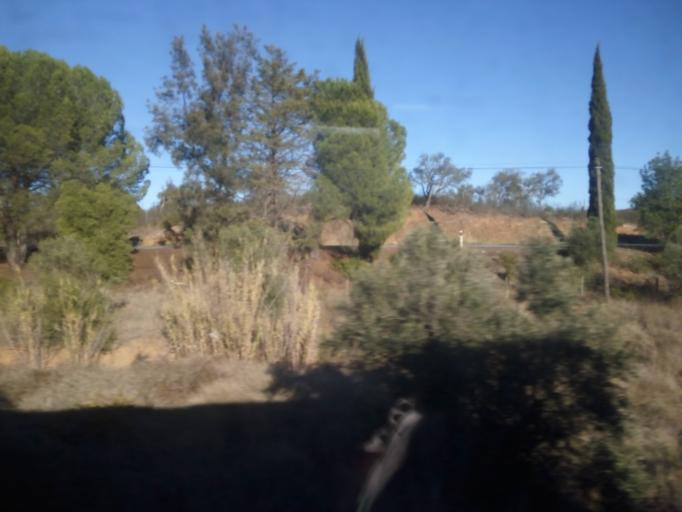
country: PT
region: Faro
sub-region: Silves
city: Sao Bartolomeu de Messines
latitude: 37.3102
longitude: -8.3181
